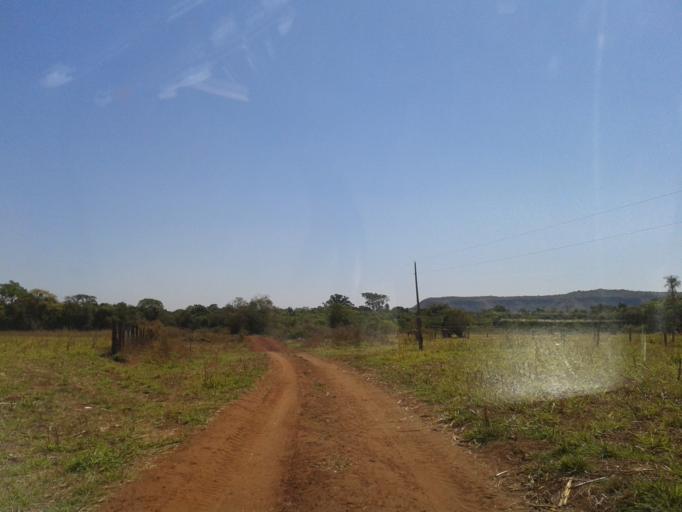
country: BR
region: Minas Gerais
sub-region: Santa Vitoria
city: Santa Vitoria
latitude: -19.0791
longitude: -50.0250
